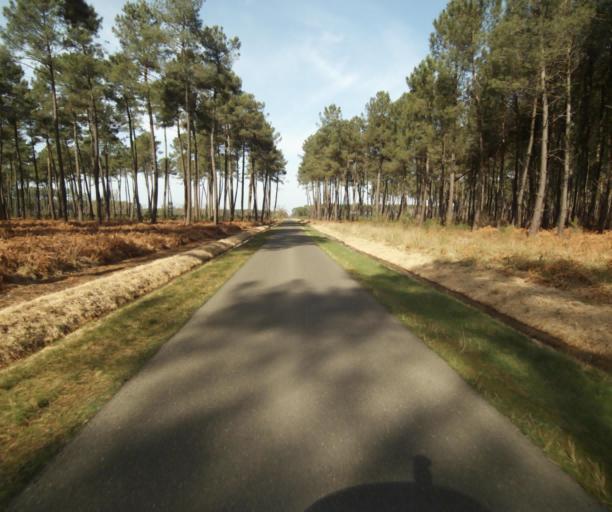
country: FR
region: Aquitaine
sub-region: Departement des Landes
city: Roquefort
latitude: 44.1948
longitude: -0.1946
